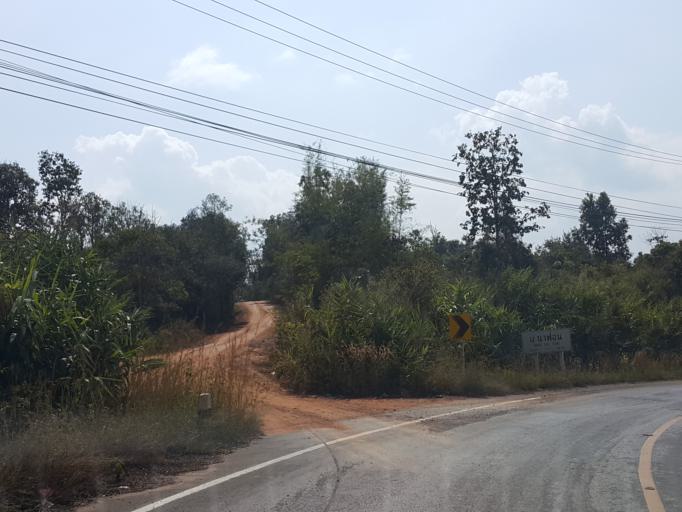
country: TH
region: Chiang Mai
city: Hot
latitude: 18.0956
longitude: 98.3750
